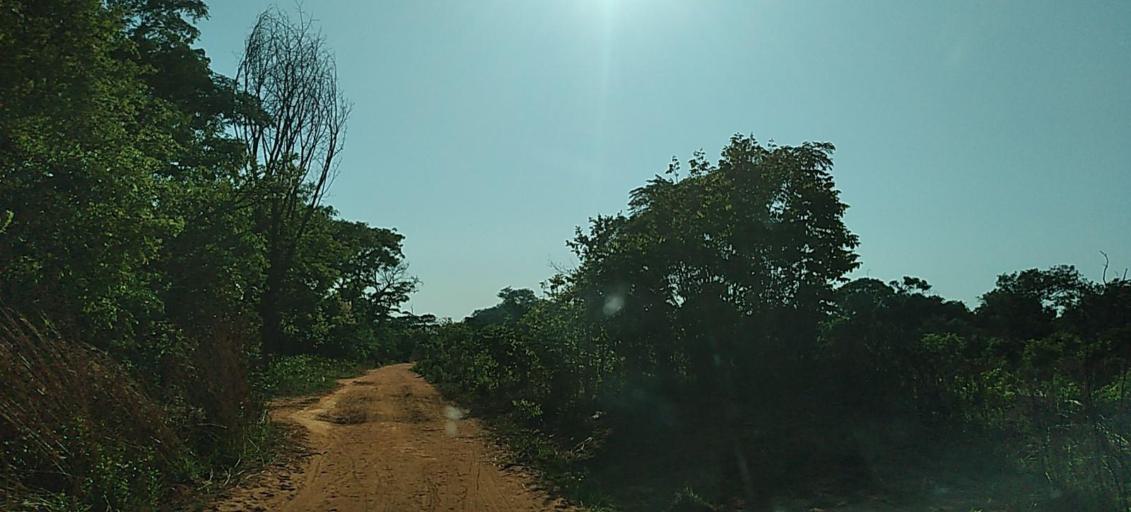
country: ZM
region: Copperbelt
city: Luanshya
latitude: -13.4591
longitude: 28.8213
